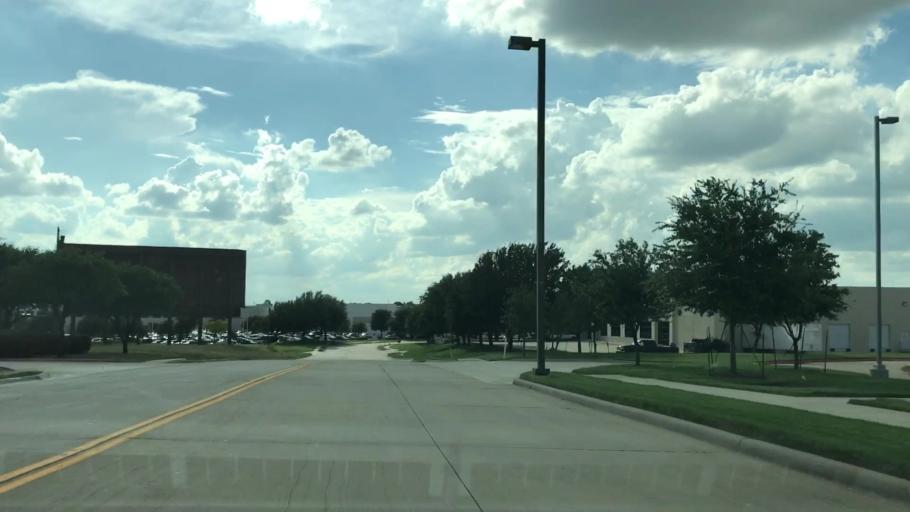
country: US
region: Texas
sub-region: Dallas County
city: Coppell
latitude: 32.9150
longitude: -97.0008
